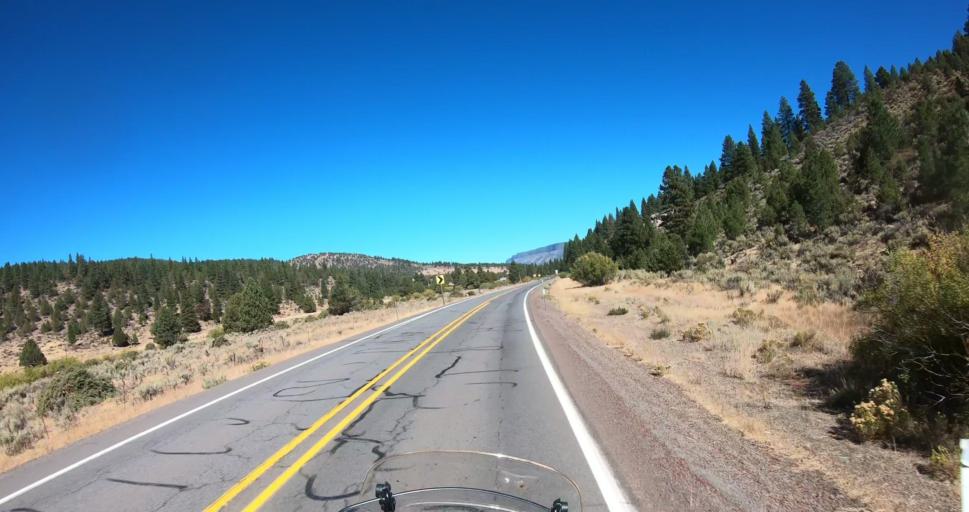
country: US
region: Oregon
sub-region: Lake County
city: Lakeview
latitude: 42.3863
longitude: -120.3057
